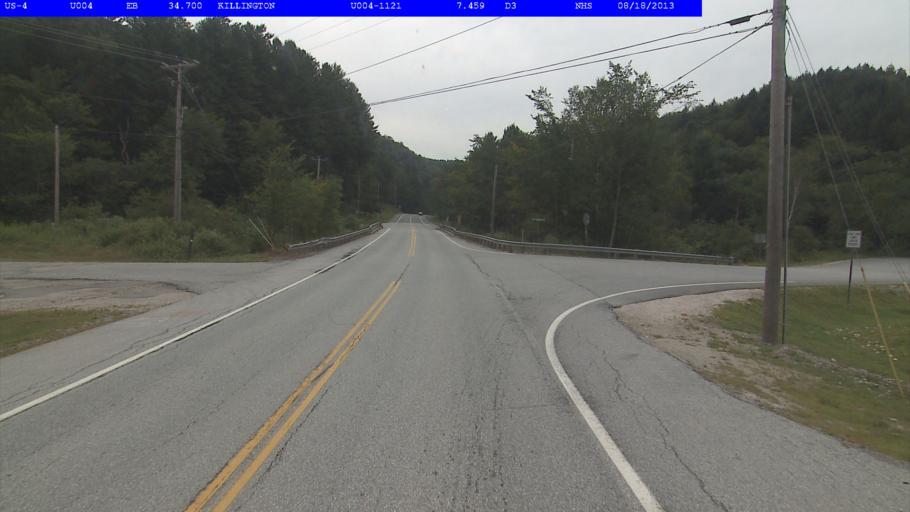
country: US
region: Vermont
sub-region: Rutland County
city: Rutland
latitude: 43.6141
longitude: -72.7556
